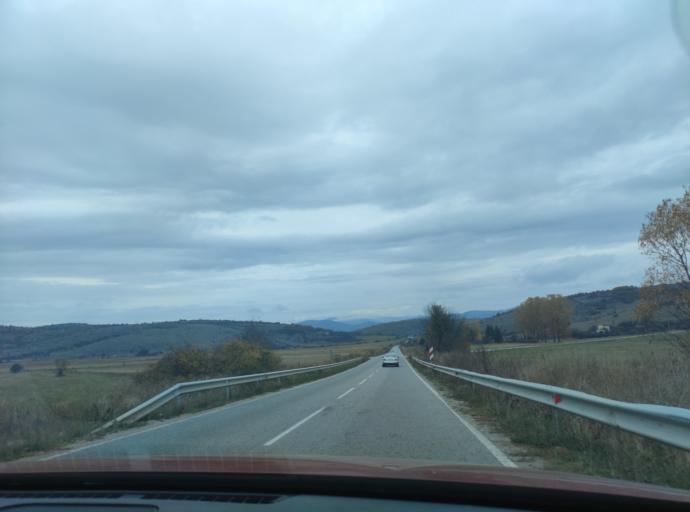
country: BG
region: Sofiya
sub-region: Obshtina Godech
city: Godech
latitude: 42.9472
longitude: 23.1600
